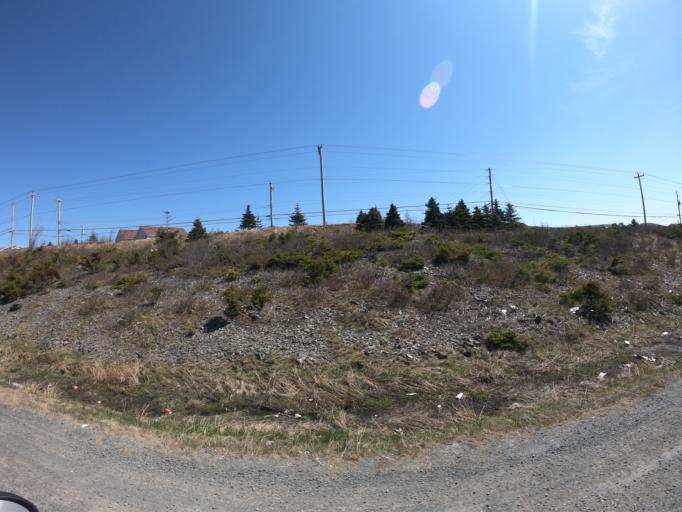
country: CA
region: Newfoundland and Labrador
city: Mount Pearl
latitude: 47.5050
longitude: -52.8207
